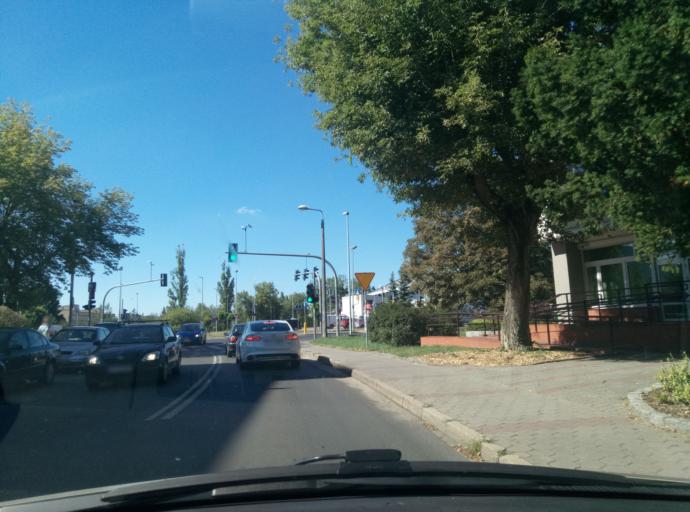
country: PL
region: Kujawsko-Pomorskie
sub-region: Torun
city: Torun
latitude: 53.0178
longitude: 18.5914
